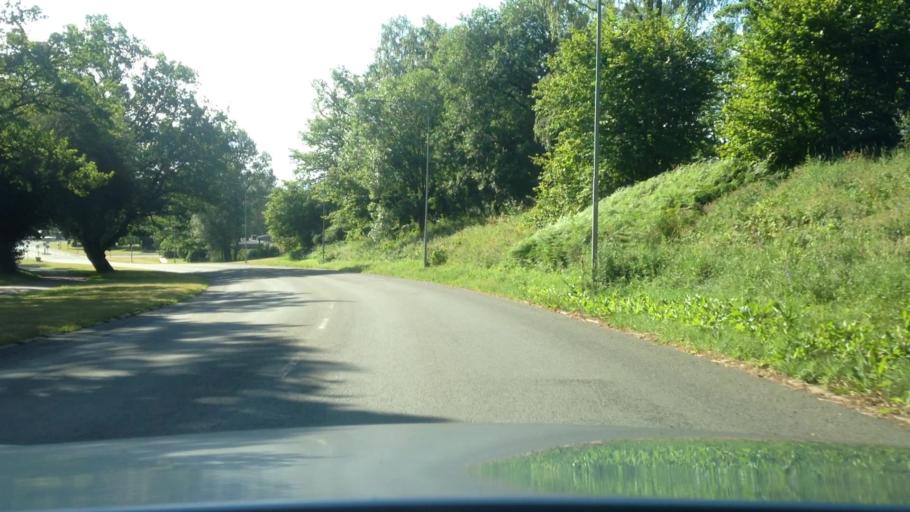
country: SE
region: Vaestra Goetaland
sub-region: Skovde Kommun
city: Skoevde
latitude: 58.3961
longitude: 13.8192
